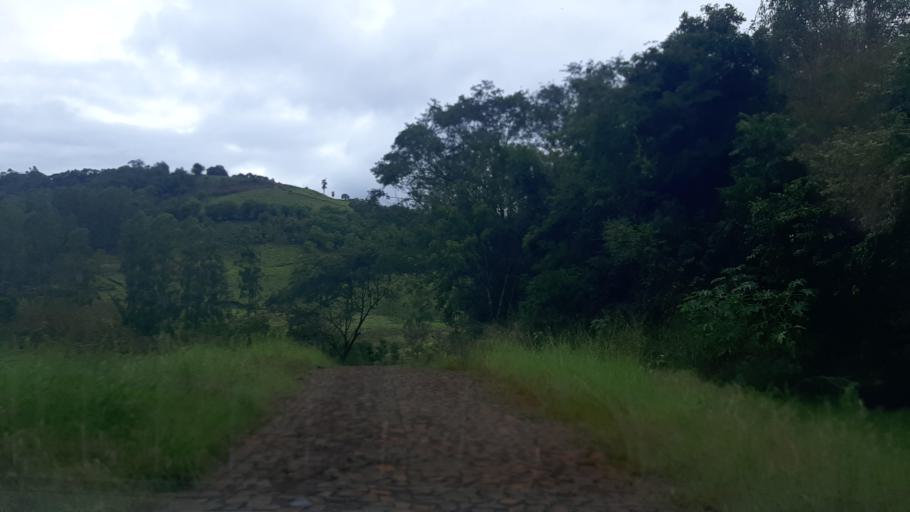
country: BR
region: Parana
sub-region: Ampere
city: Ampere
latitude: -26.0448
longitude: -53.5154
